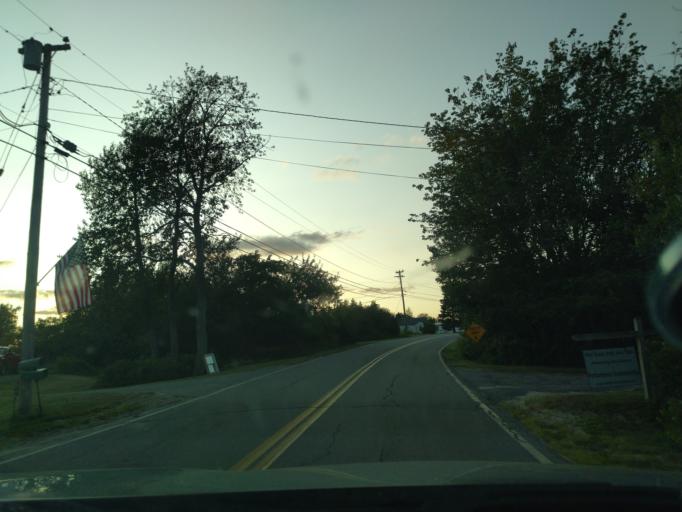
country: US
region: Maine
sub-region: Hancock County
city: Gouldsboro
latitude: 44.3861
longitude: -68.0388
